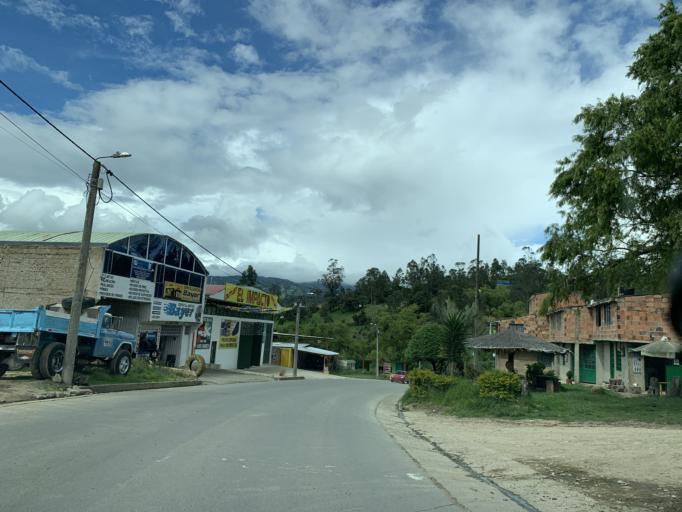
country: CO
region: Boyaca
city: Ramiriqui
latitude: 5.4083
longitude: -73.3335
